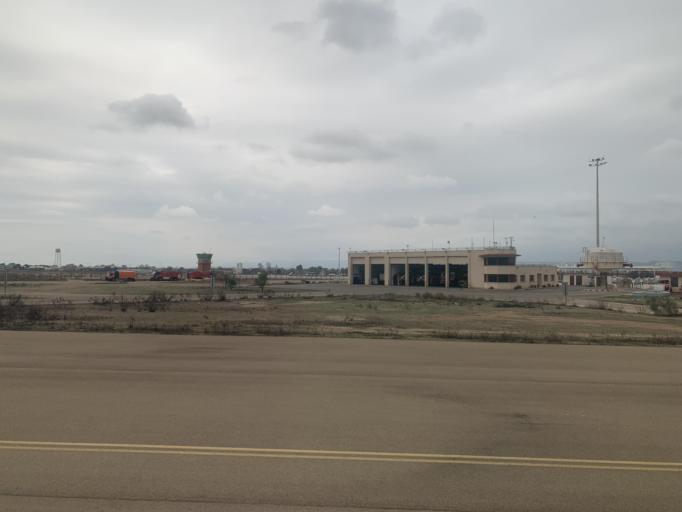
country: ES
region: Aragon
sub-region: Provincia de Zaragoza
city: Utebo
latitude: 41.6617
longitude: -1.0133
